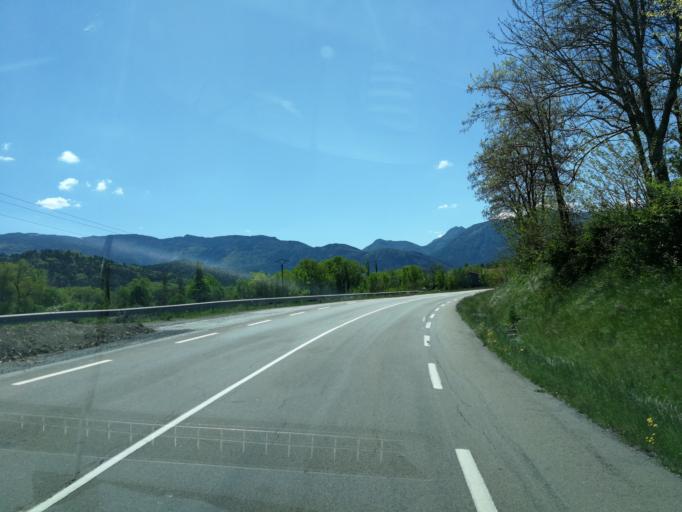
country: FR
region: Rhone-Alpes
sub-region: Departement de la Drome
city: Die
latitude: 44.7328
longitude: 5.2678
